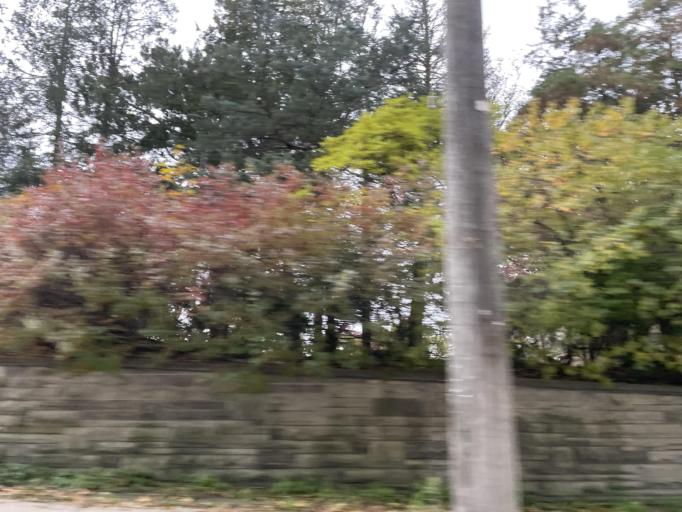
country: CA
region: Ontario
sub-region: Wellington County
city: Guelph
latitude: 43.5348
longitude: -80.2365
